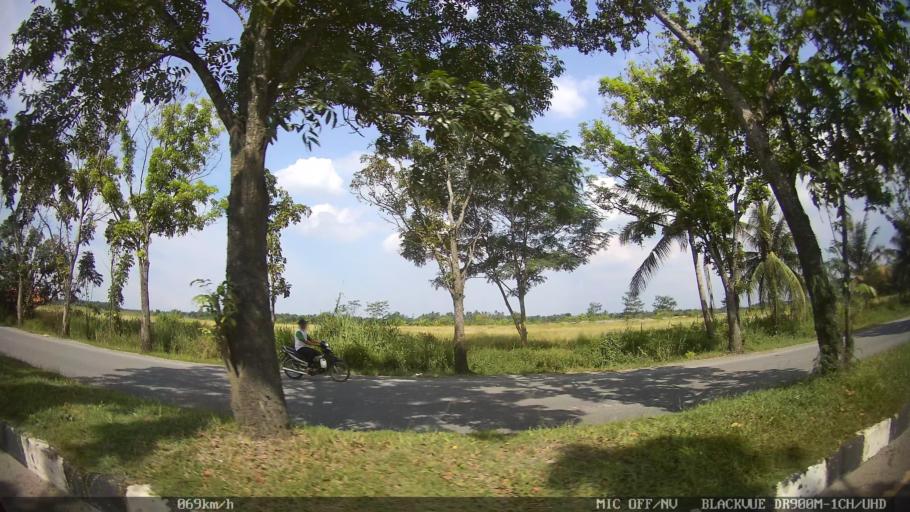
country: ID
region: North Sumatra
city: Binjai
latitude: 3.6243
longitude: 98.5348
